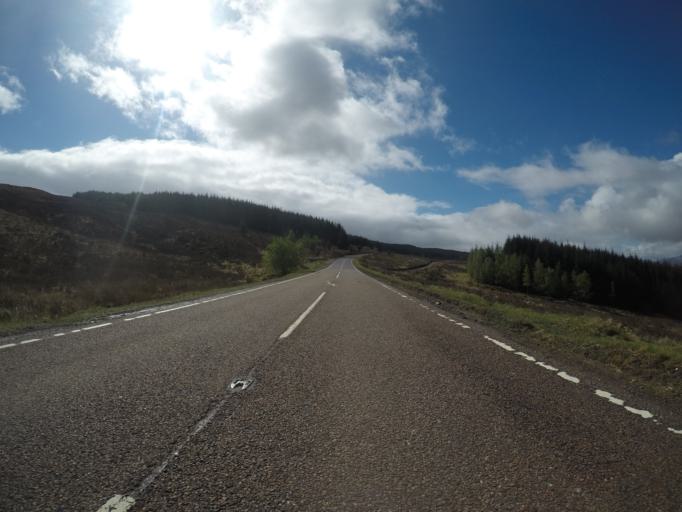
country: GB
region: Scotland
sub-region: Highland
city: Spean Bridge
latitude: 57.1135
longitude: -4.9836
